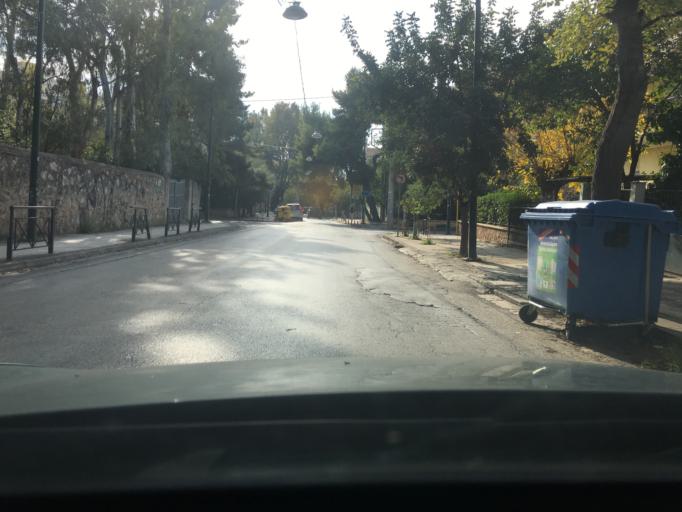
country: GR
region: Attica
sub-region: Nomarchia Athinas
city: Khalandrion
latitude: 38.0295
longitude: 23.7975
